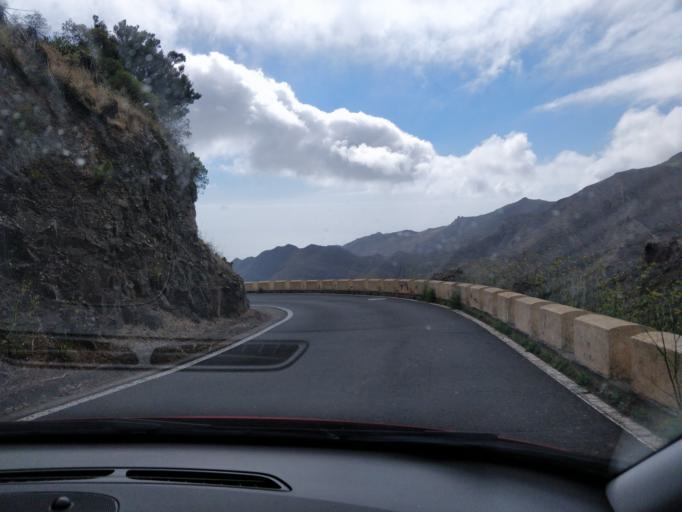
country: ES
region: Canary Islands
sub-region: Provincia de Santa Cruz de Tenerife
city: Tanque
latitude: 28.3254
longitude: -16.8559
